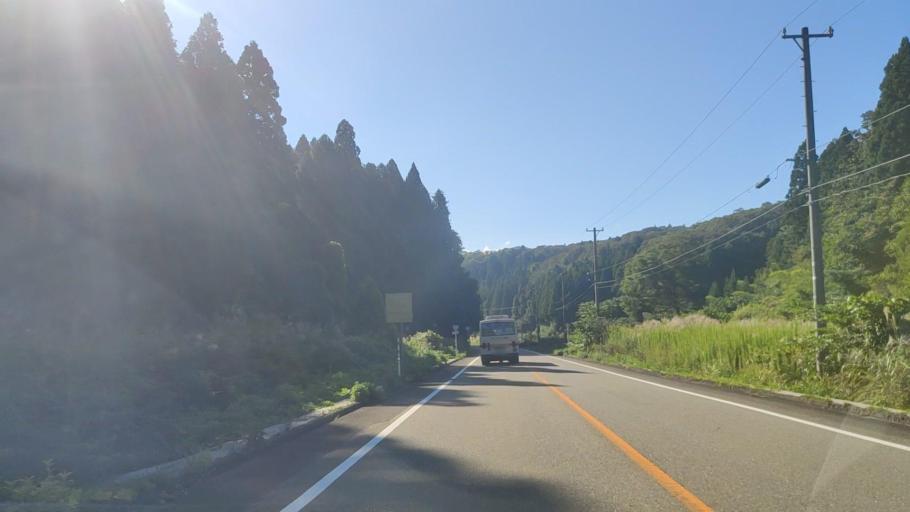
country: JP
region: Ishikawa
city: Nanao
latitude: 37.2416
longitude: 136.9850
